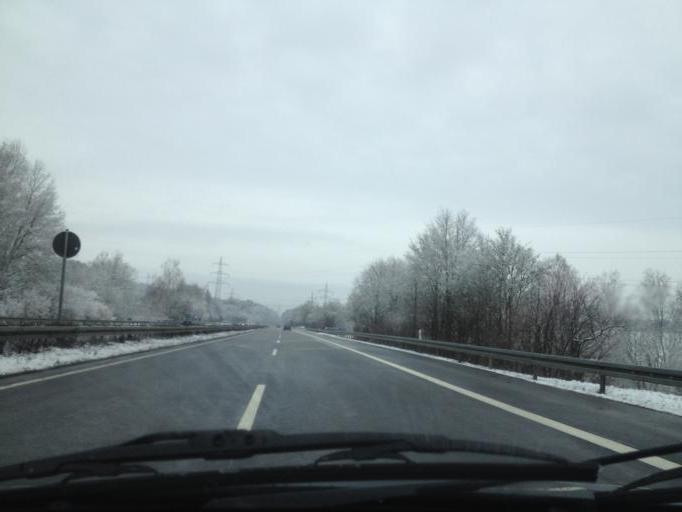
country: DE
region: Saarland
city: Homburg
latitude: 49.2990
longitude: 7.2923
